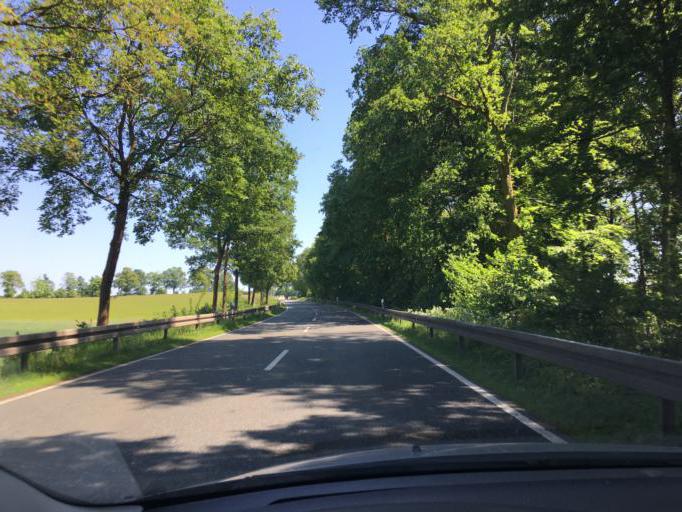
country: DE
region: Thuringia
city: Grossensee
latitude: 50.9390
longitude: 9.9197
